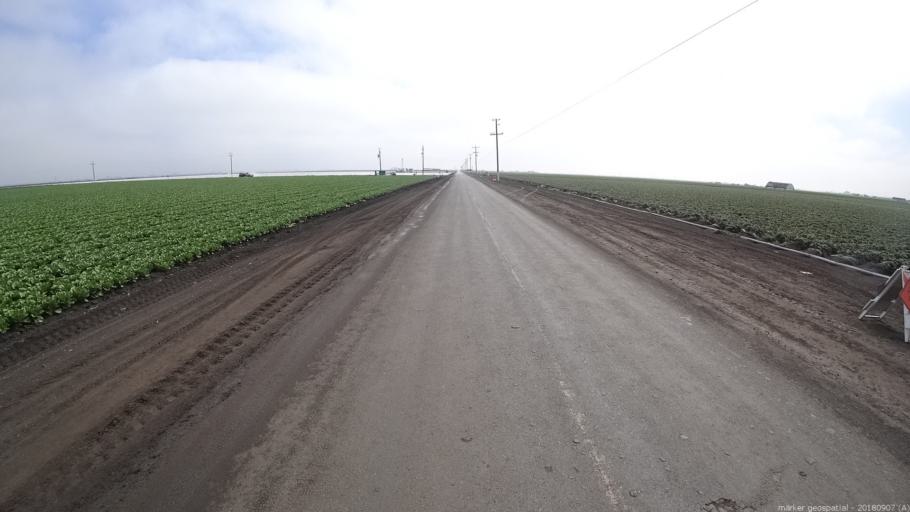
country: US
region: California
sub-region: Monterey County
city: Boronda
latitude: 36.6933
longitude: -121.7275
